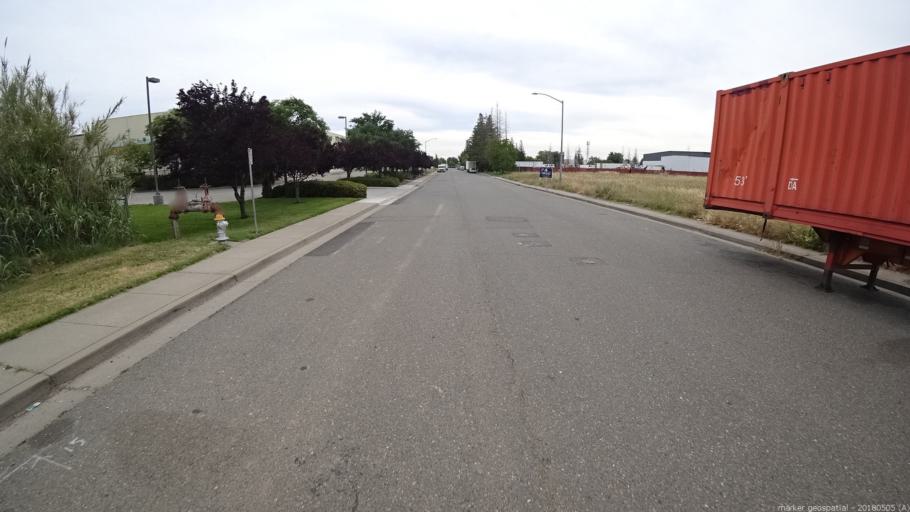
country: US
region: California
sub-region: Sacramento County
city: Rio Linda
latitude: 38.6492
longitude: -121.4281
